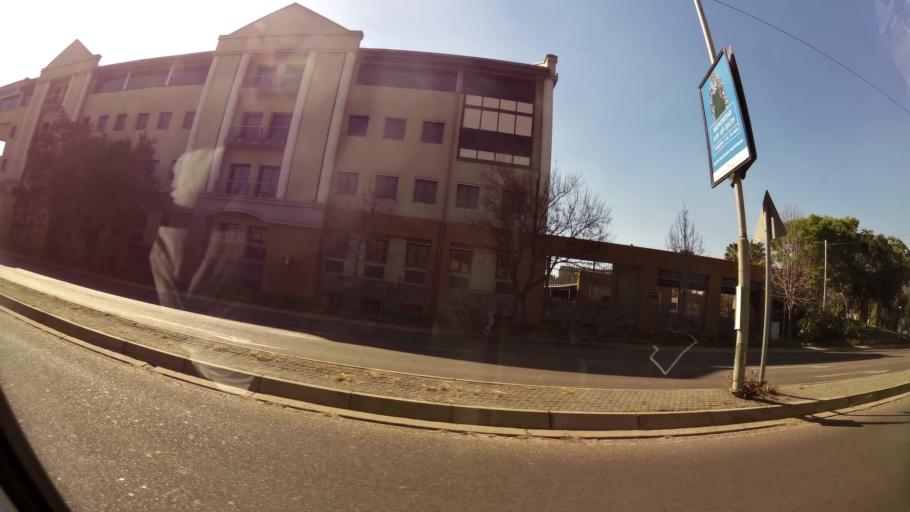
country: ZA
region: Gauteng
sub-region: City of Tshwane Metropolitan Municipality
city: Pretoria
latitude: -25.7723
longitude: 28.2361
